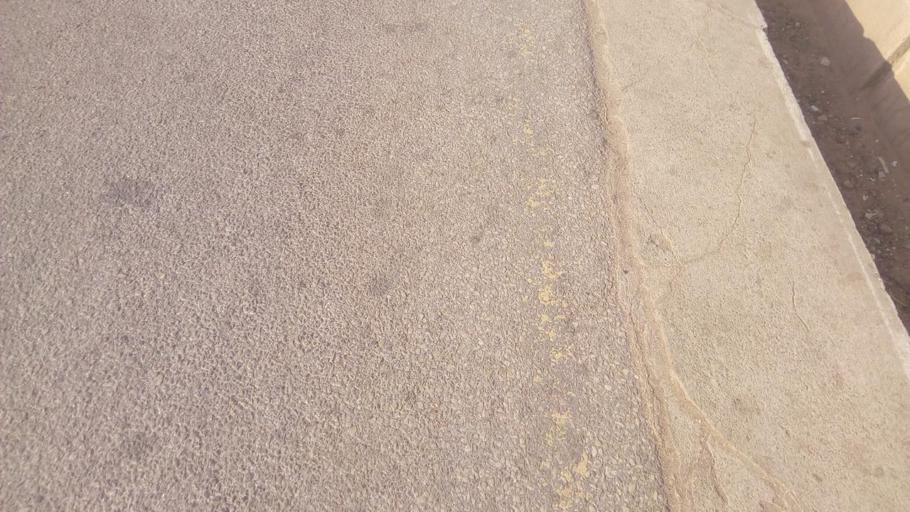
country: ZM
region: Lusaka
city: Lusaka
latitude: -15.3627
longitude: 28.3038
